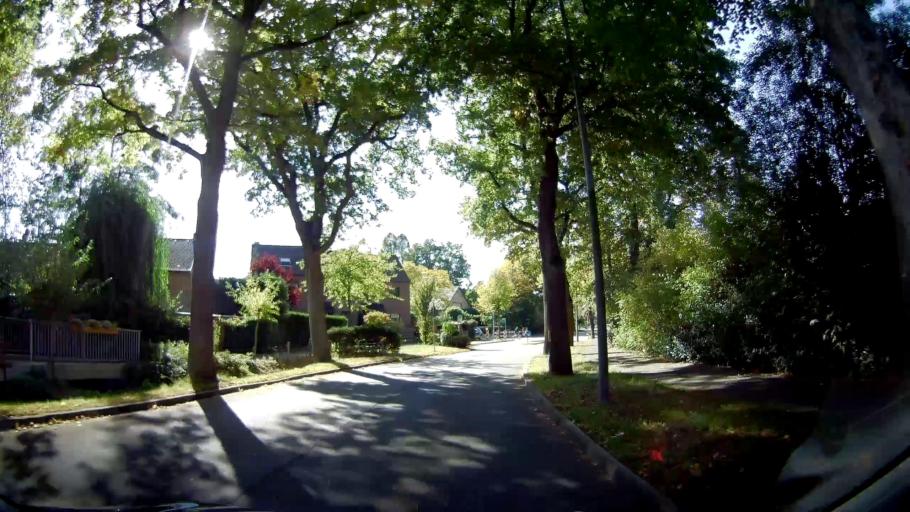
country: DE
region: North Rhine-Westphalia
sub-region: Regierungsbezirk Dusseldorf
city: Hunxe
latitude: 51.6387
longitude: 6.7659
